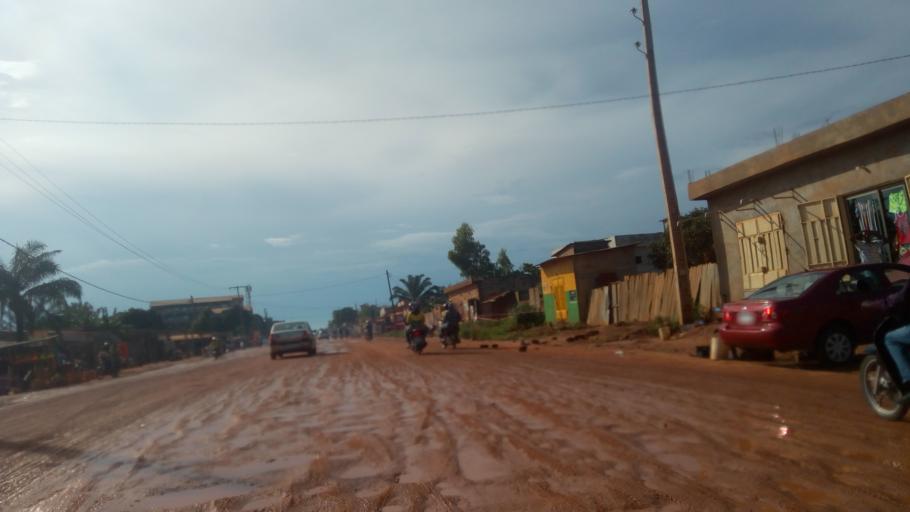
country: BJ
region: Atlantique
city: Abomey-Calavi
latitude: 6.4544
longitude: 2.3335
